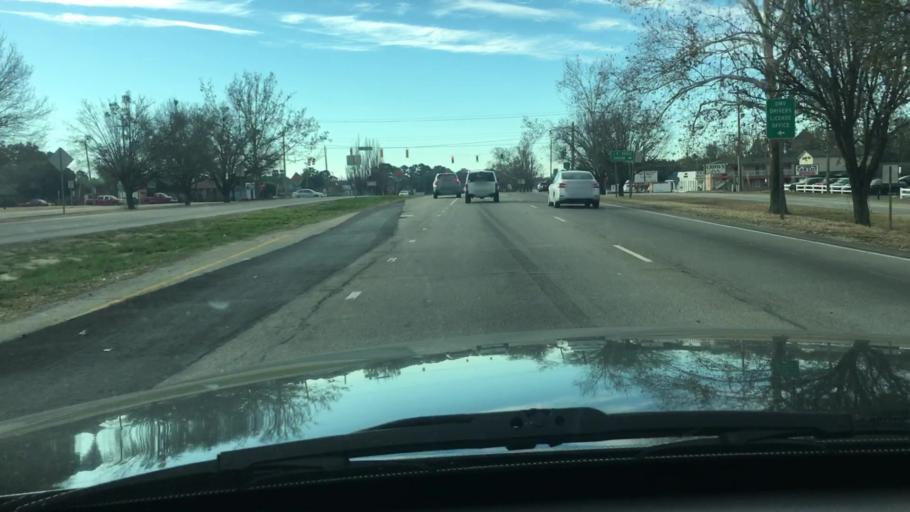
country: US
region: North Carolina
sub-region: Cumberland County
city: Fayetteville
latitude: 35.0143
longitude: -78.8971
